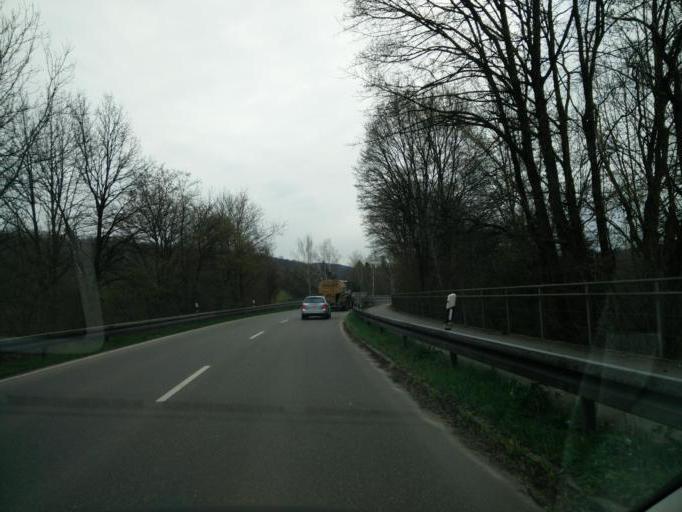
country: DE
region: Baden-Wuerttemberg
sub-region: Tuebingen Region
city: Kusterdingen
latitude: 48.5315
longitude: 9.1319
